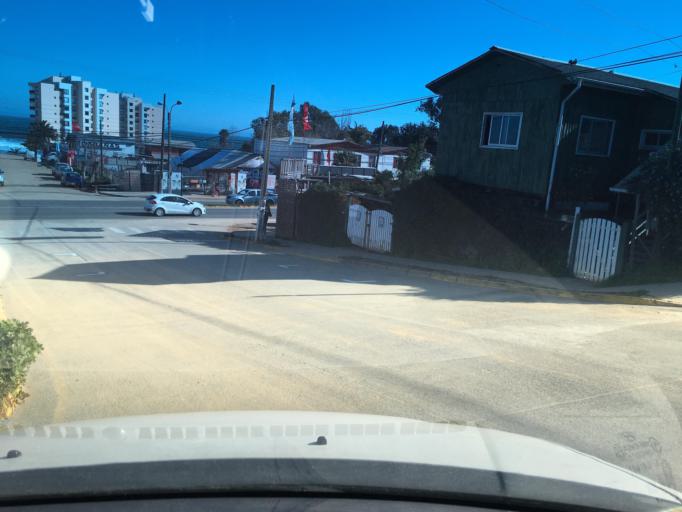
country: CL
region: Valparaiso
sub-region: San Antonio Province
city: El Tabo
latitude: -33.4565
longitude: -71.6616
